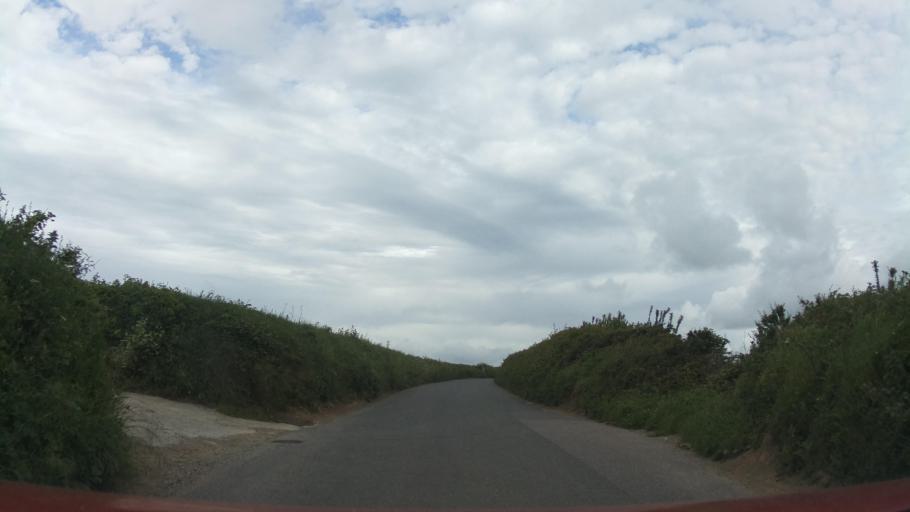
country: GB
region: England
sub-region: Devon
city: Dartmouth
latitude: 50.3377
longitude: -3.6518
